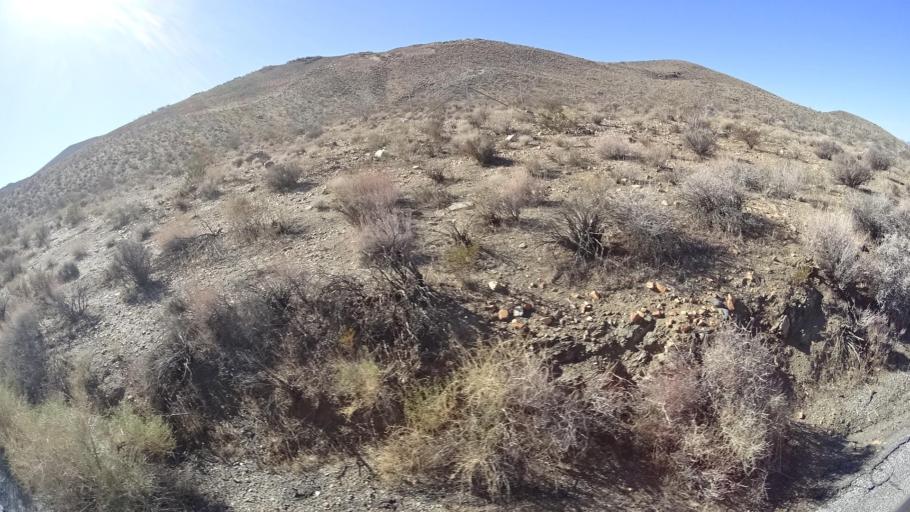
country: US
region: California
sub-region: Kern County
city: Ridgecrest
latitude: 35.3744
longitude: -117.6621
